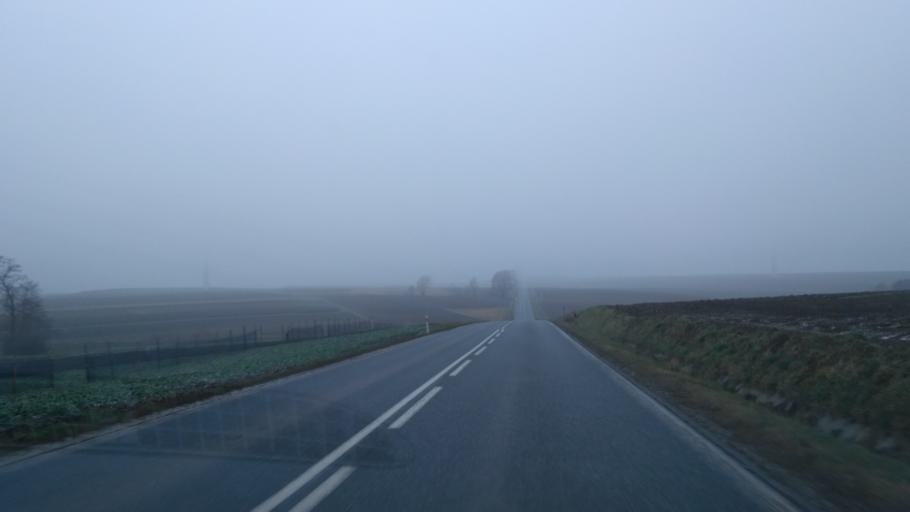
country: PL
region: Subcarpathian Voivodeship
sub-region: Powiat lancucki
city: Markowa
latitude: 50.0429
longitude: 22.3037
